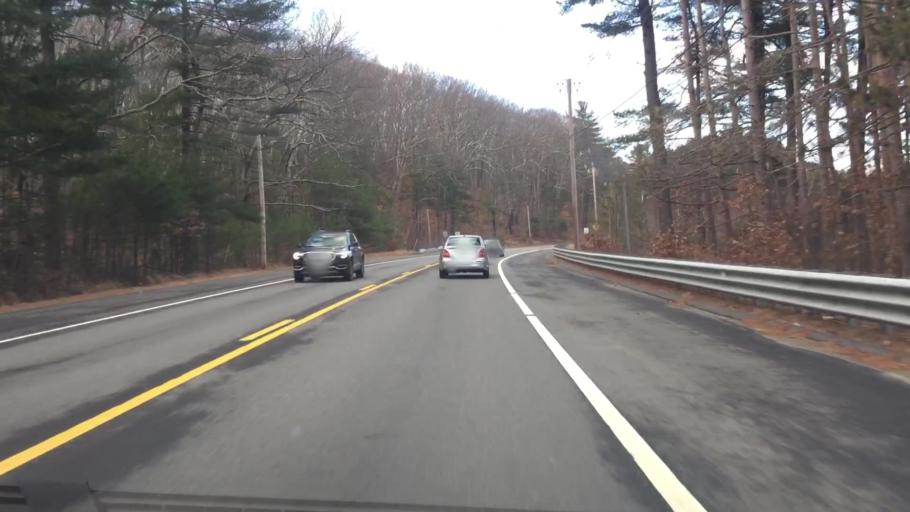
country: US
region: Massachusetts
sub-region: Worcester County
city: West Boylston
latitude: 42.3444
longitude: -71.7617
